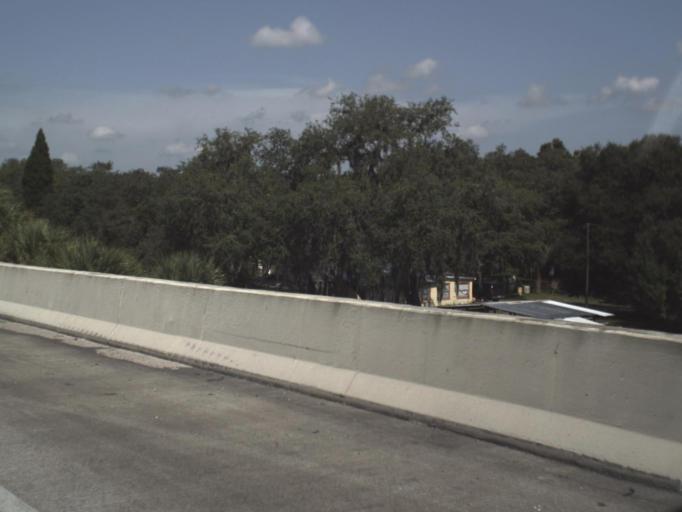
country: US
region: Florida
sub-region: Hillsborough County
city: Plant City
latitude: 28.0372
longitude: -82.0723
